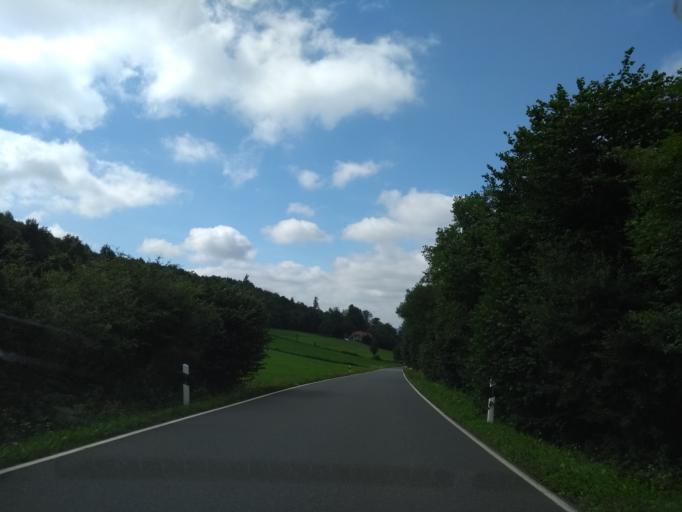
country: DE
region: North Rhine-Westphalia
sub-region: Regierungsbezirk Detmold
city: Lugde
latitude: 51.9515
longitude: 9.2664
